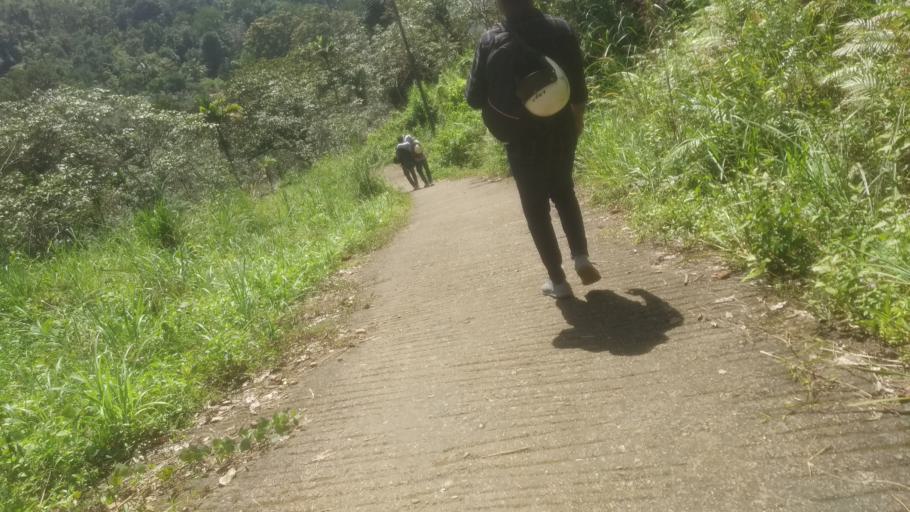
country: IN
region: Kerala
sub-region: Idukki
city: Idukki
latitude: 9.9747
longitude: 76.8380
